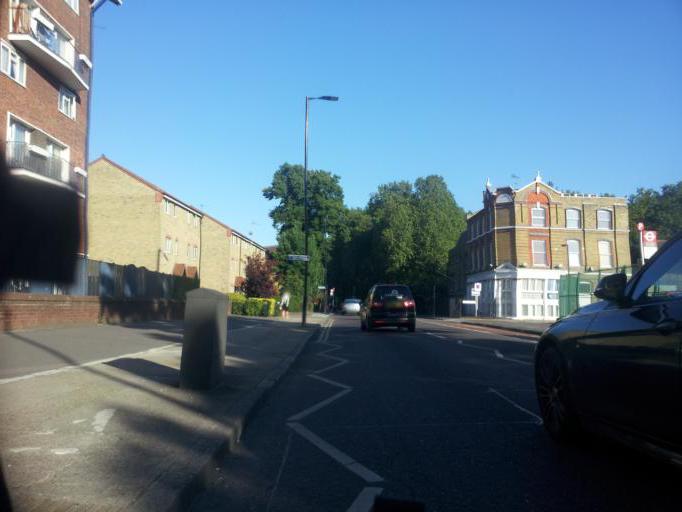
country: GB
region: England
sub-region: Greater London
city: Bethnal Green
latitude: 51.4957
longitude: -0.0514
